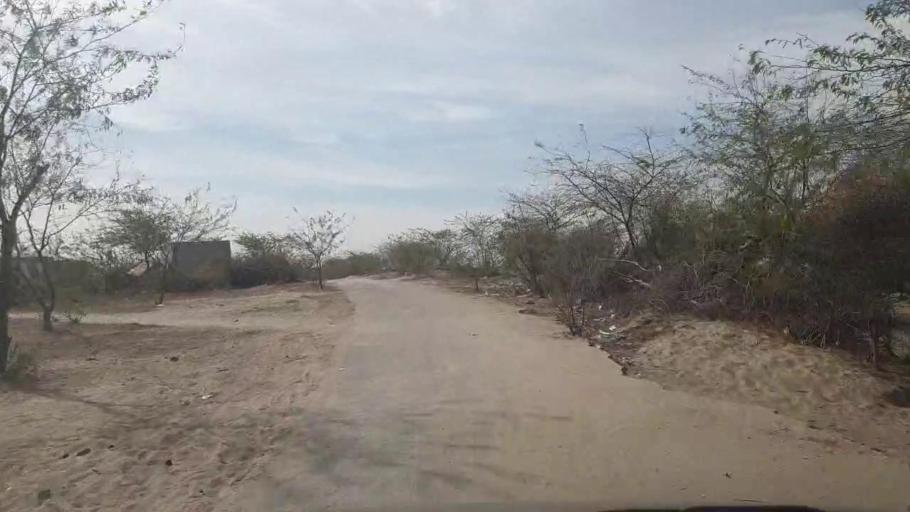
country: PK
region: Sindh
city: Umarkot
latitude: 25.2779
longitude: 69.7443
